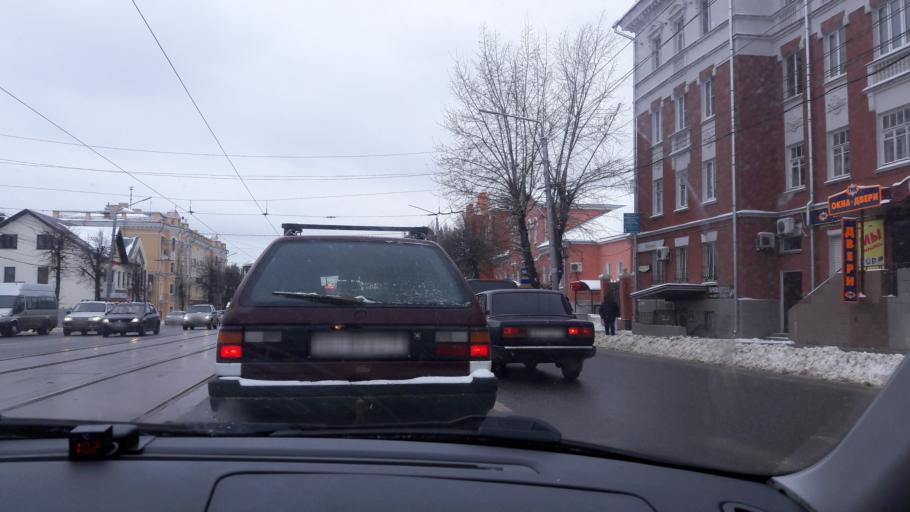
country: RU
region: Tula
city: Tula
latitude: 54.2101
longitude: 37.6209
